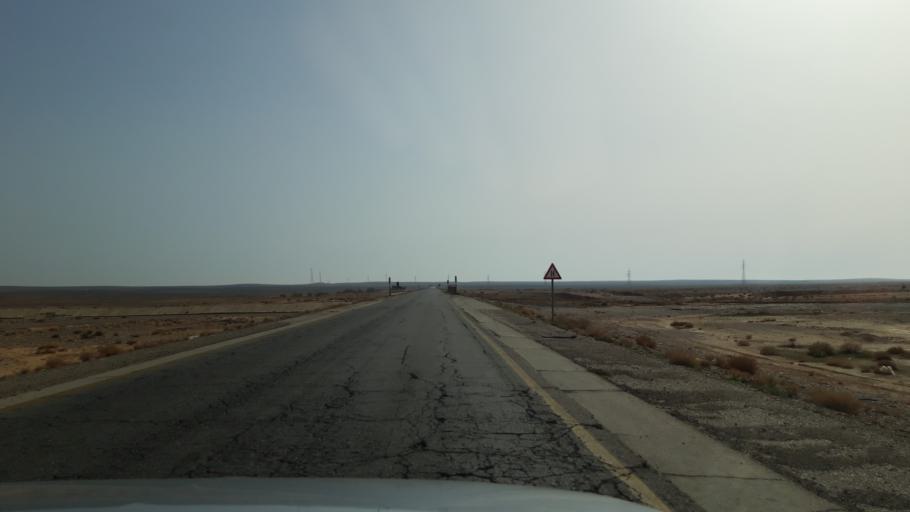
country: JO
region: Amman
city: Al Azraq ash Shamali
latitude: 31.7302
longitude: 36.4897
